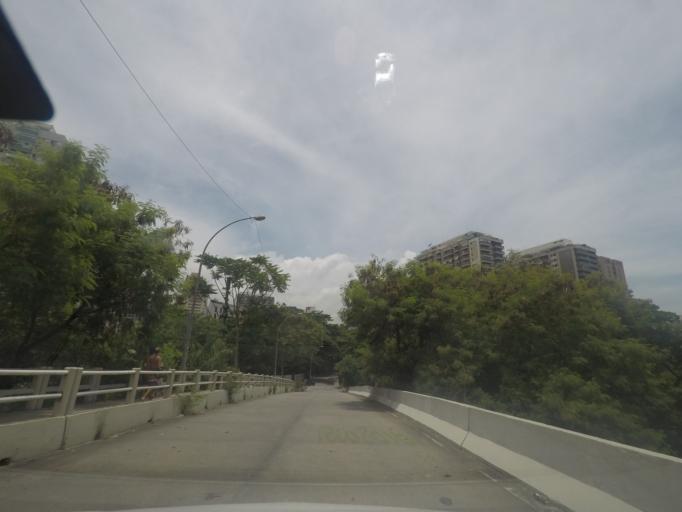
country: BR
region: Rio de Janeiro
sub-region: Rio De Janeiro
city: Rio de Janeiro
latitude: -23.0069
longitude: -43.3294
